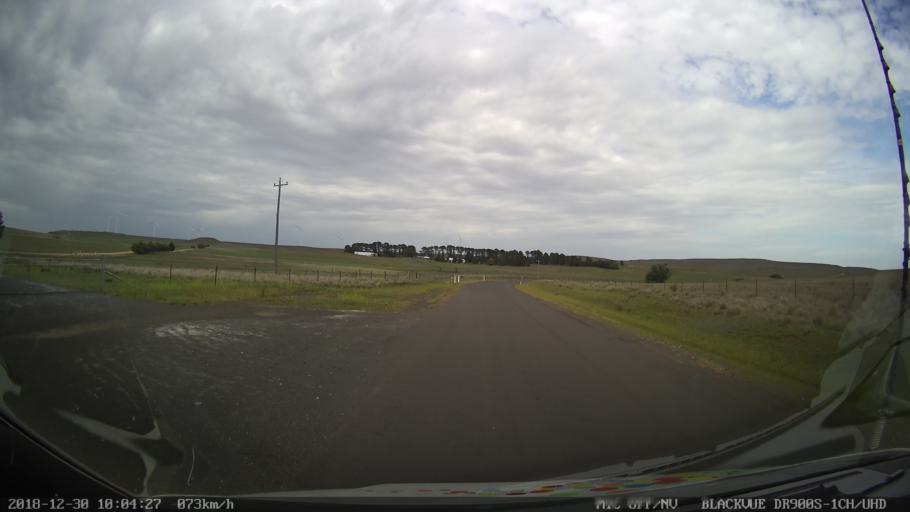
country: AU
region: New South Wales
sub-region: Cooma-Monaro
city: Cooma
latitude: -36.5220
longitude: 149.1462
